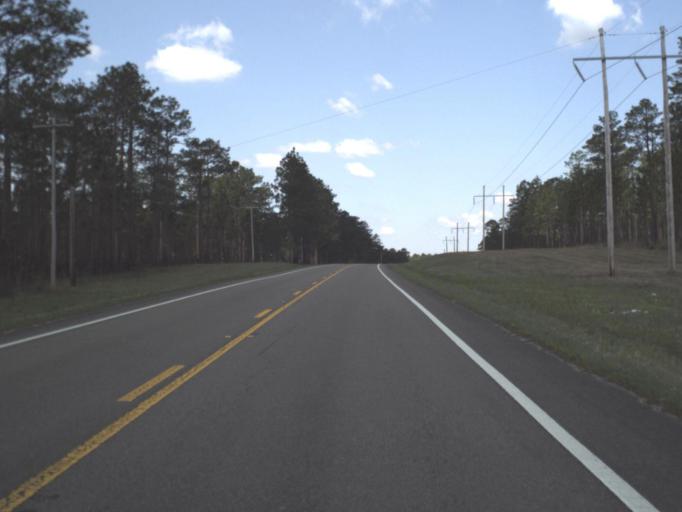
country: US
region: Florida
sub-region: Santa Rosa County
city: Point Baker
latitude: 30.8719
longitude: -86.9336
